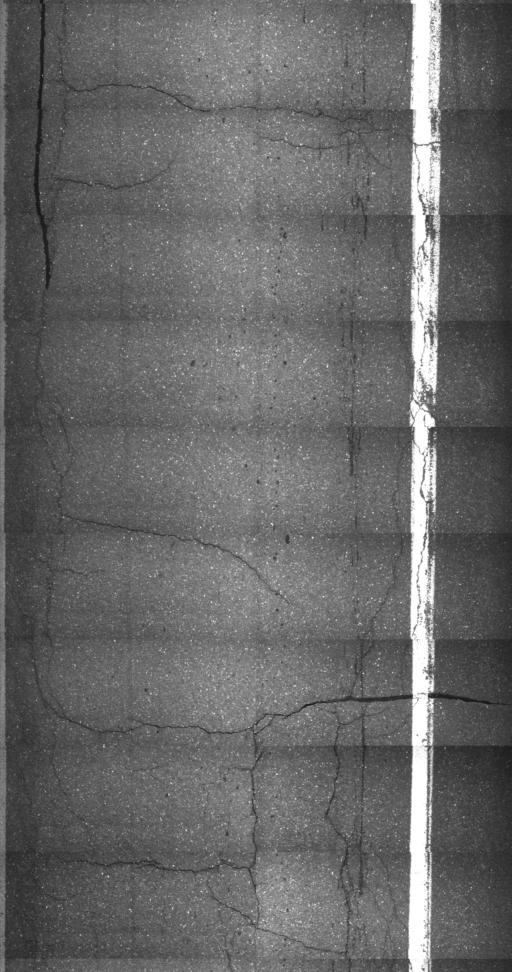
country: US
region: Vermont
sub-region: Caledonia County
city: Saint Johnsbury
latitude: 44.2917
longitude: -72.0582
